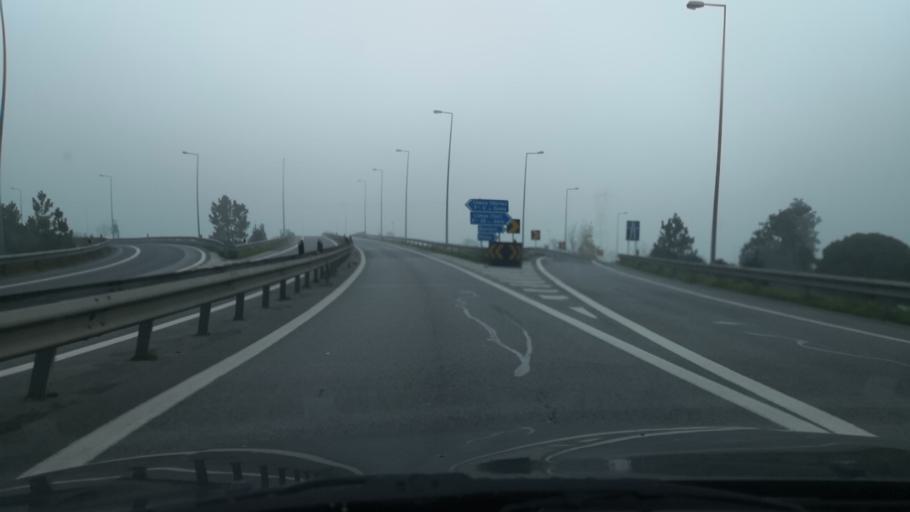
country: PT
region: Setubal
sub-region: Montijo
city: Montijo
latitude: 38.6801
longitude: -8.9468
